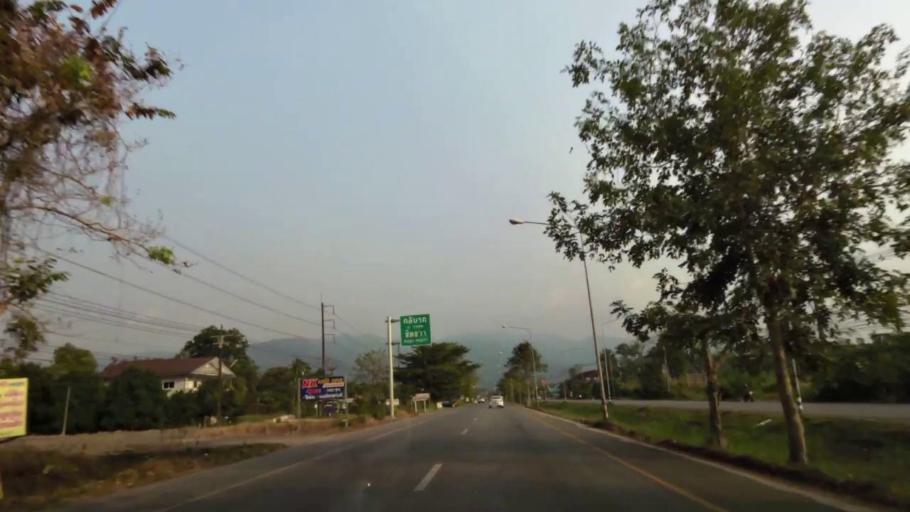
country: TH
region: Chanthaburi
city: Chanthaburi
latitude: 12.5942
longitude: 102.1461
